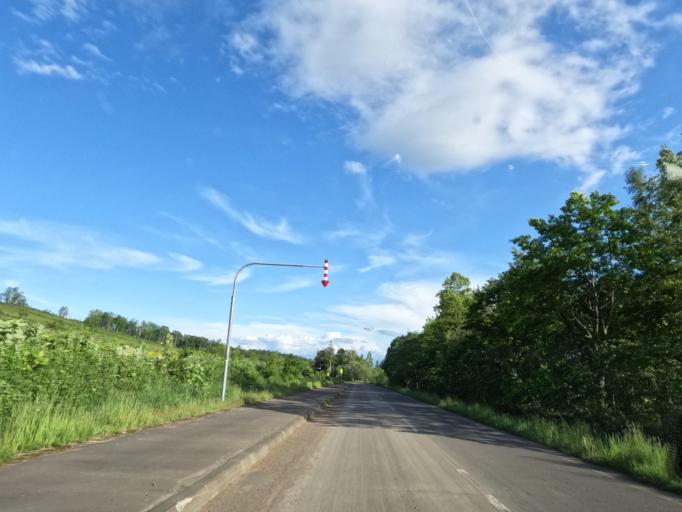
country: JP
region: Hokkaido
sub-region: Asahikawa-shi
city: Asahikawa
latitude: 43.9205
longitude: 142.4995
